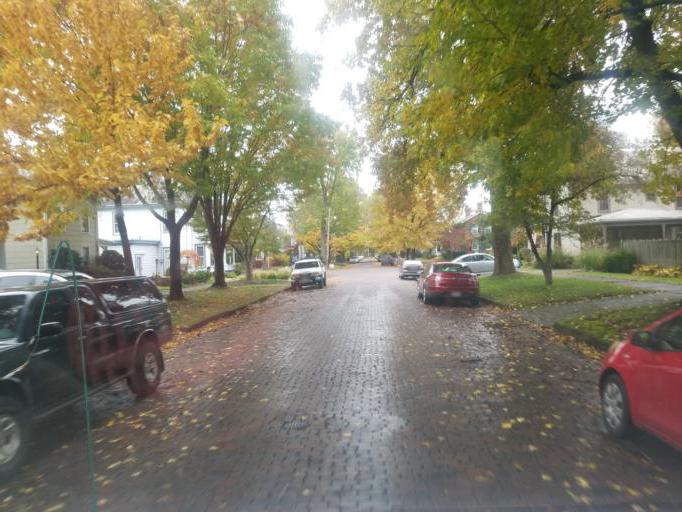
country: US
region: Ohio
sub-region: Washington County
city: Marietta
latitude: 39.4229
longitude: -81.4540
